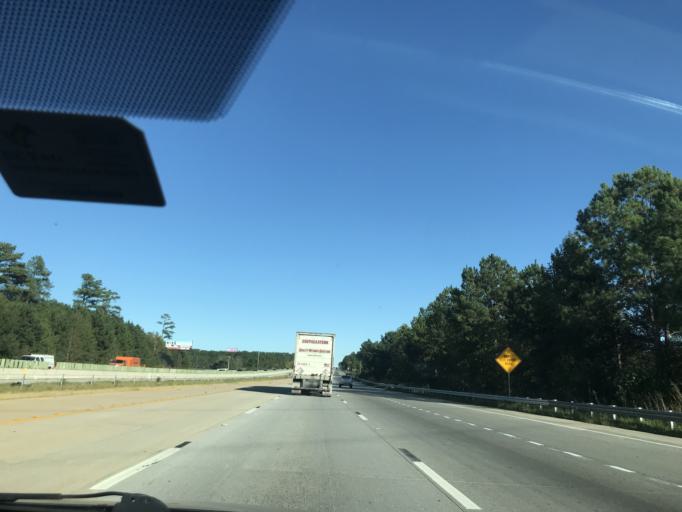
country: US
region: South Carolina
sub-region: Spartanburg County
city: Valley Falls
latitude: 35.0126
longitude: -81.9528
